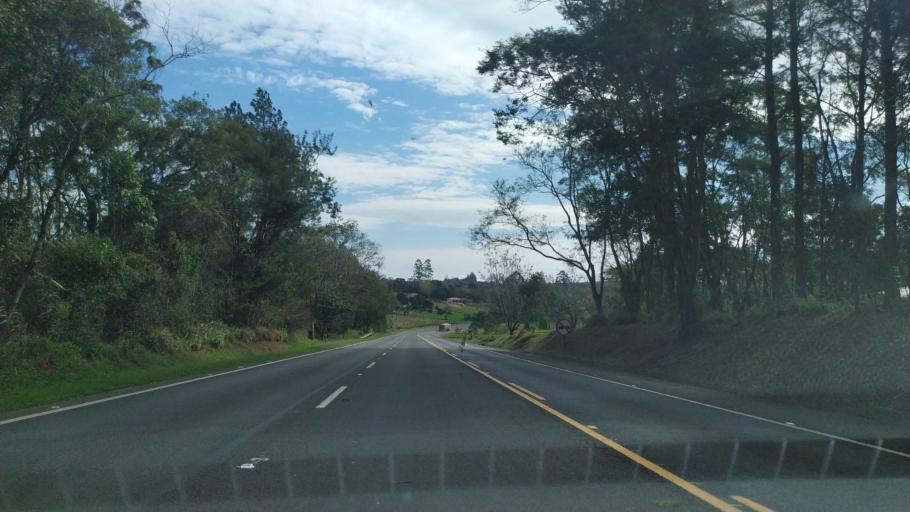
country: BR
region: Parana
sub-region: Ortigueira
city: Ortigueira
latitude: -24.2938
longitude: -50.8753
